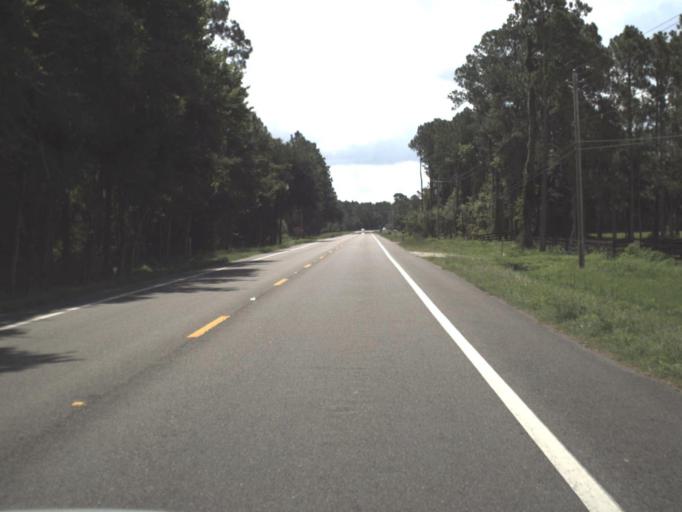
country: US
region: Florida
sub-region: Clay County
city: Green Cove Springs
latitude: 29.9778
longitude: -81.5485
